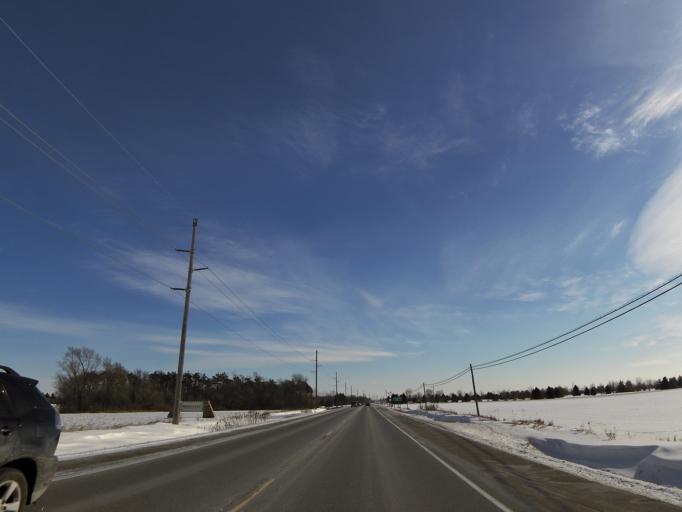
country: US
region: Minnesota
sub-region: Washington County
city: Cottage Grove
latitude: 44.7422
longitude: -92.9780
